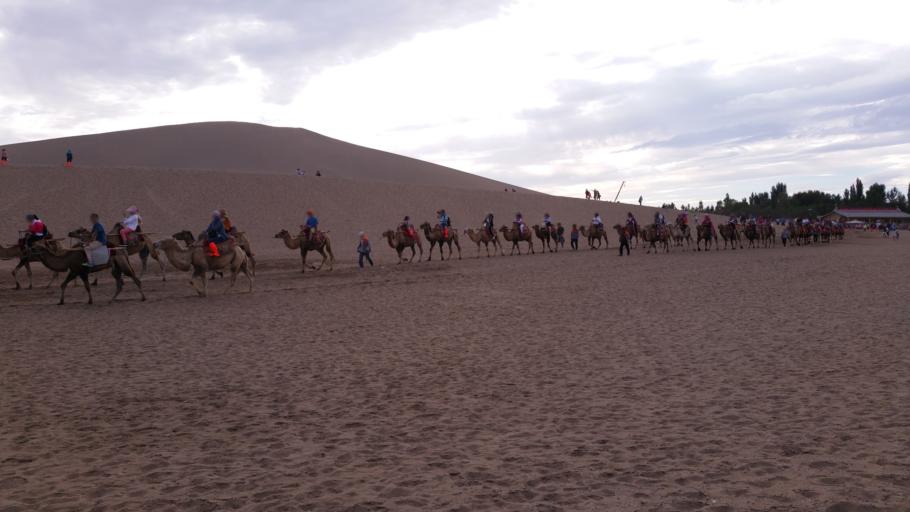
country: CN
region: Gansu Sheng
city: Yangjiaqiao
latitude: 40.0912
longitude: 94.6772
